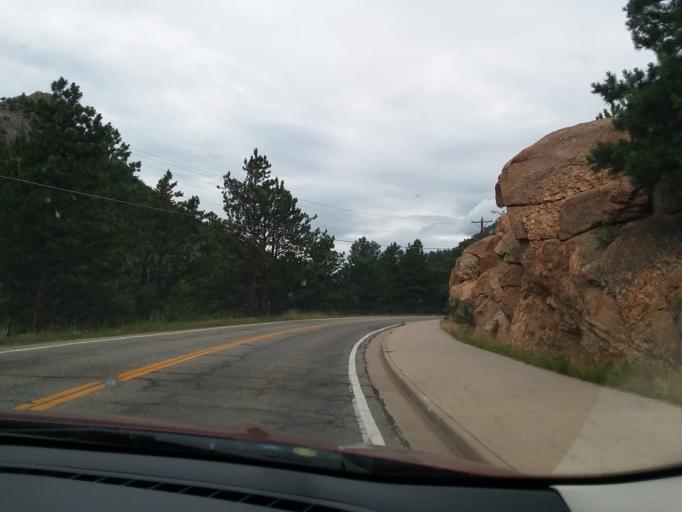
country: US
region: Colorado
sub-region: Larimer County
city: Estes Park
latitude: 40.3788
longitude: -105.5366
